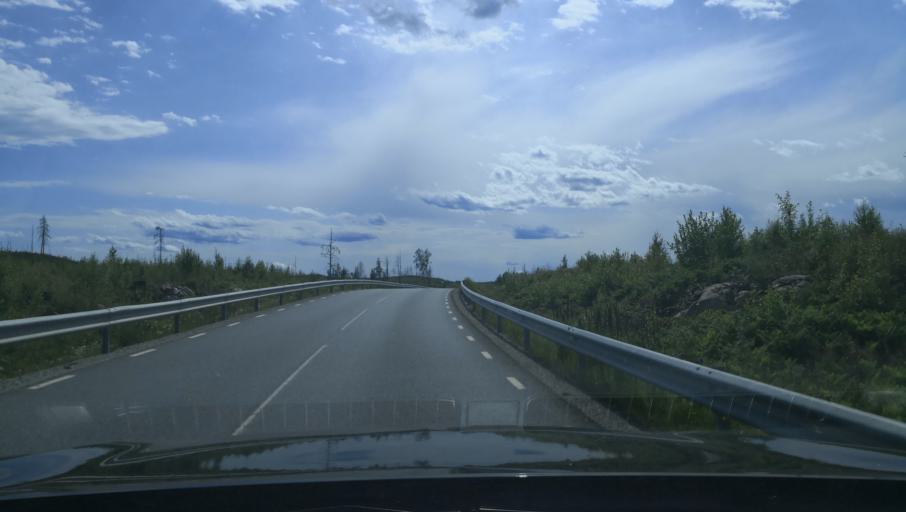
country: SE
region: Vaestmanland
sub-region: Norbergs Kommun
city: Norberg
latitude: 59.9919
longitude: 16.0660
